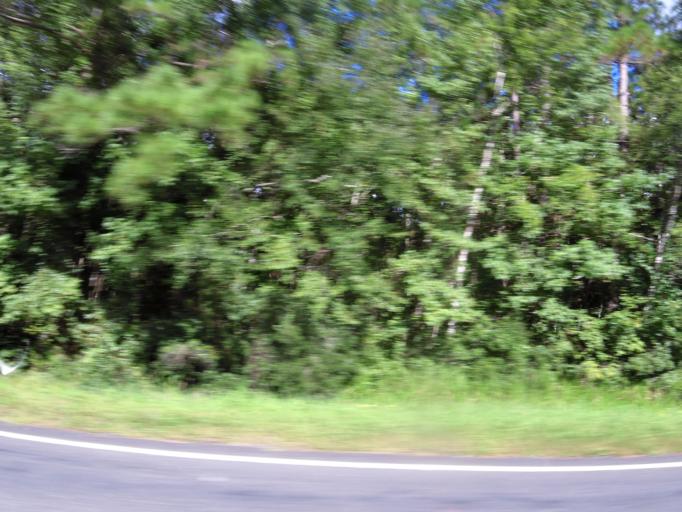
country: US
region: Georgia
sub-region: Camden County
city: Kingsland
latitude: 30.8522
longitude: -81.7006
